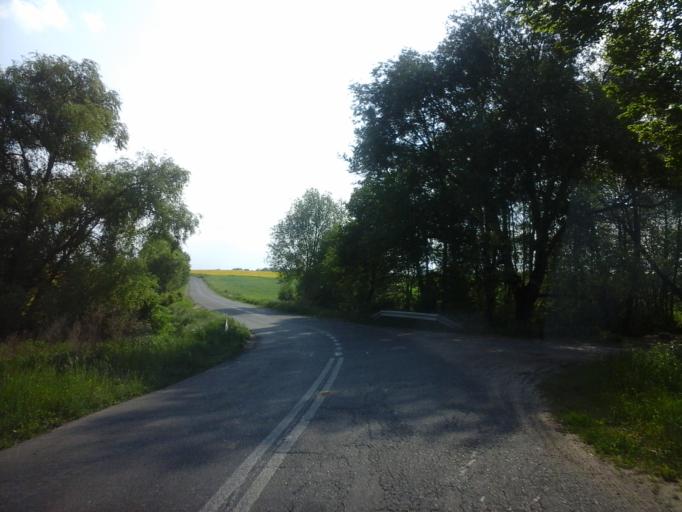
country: PL
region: West Pomeranian Voivodeship
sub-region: Powiat choszczenski
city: Pelczyce
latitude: 53.0542
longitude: 15.3182
